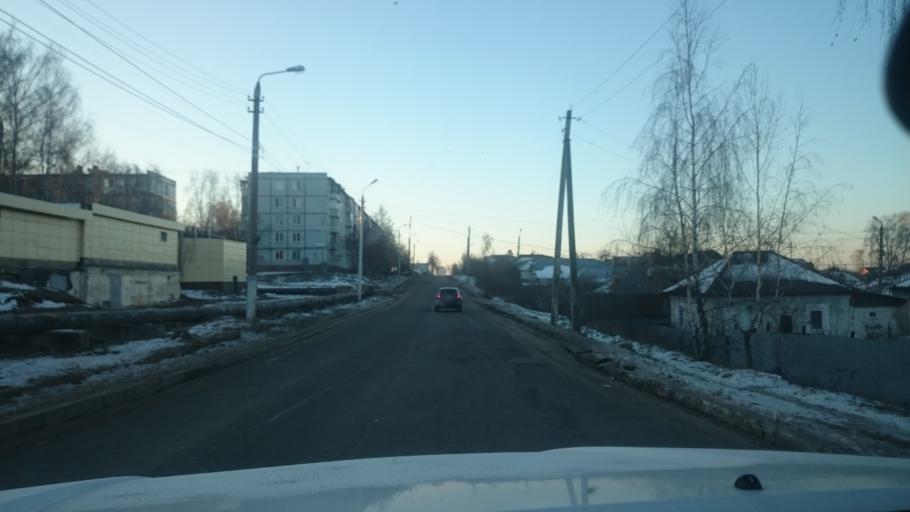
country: RU
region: Tula
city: Tula
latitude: 54.2071
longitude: 37.6976
